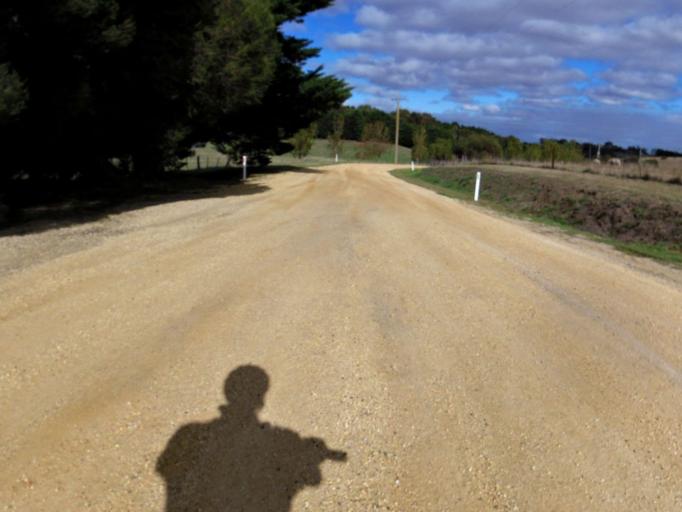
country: AU
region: Victoria
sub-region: Greater Geelong
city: Wandana Heights
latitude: -38.1814
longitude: 144.2988
